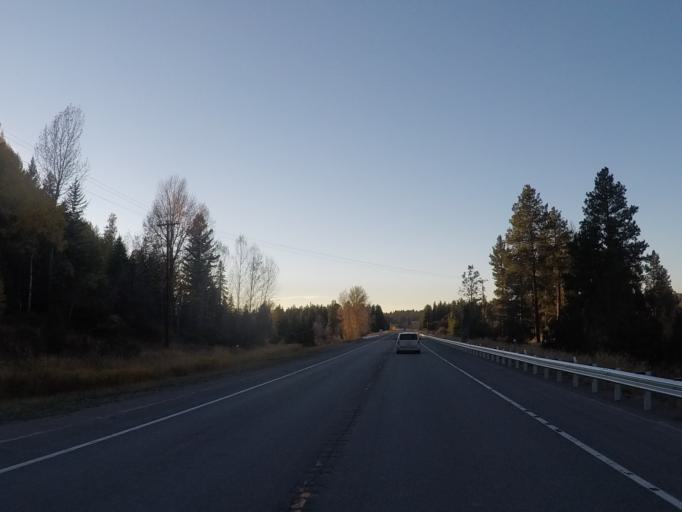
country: US
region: Montana
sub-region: Lewis and Clark County
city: Lincoln
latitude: 46.9992
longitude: -113.0341
